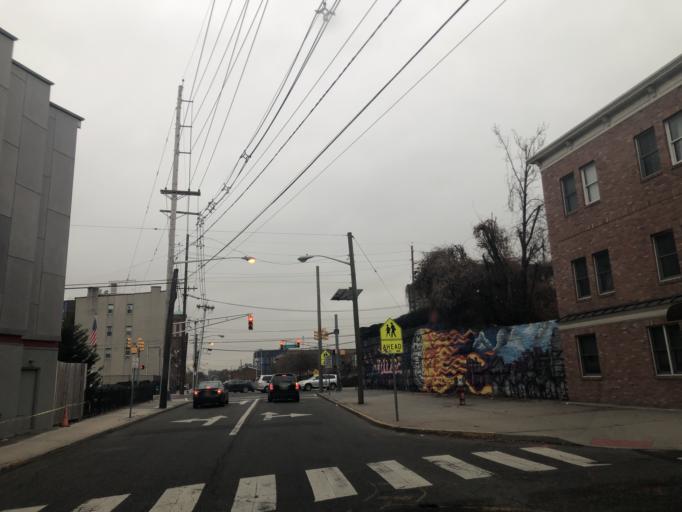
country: US
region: New Jersey
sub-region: Hudson County
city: Jersey City
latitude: 40.7224
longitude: -74.0509
